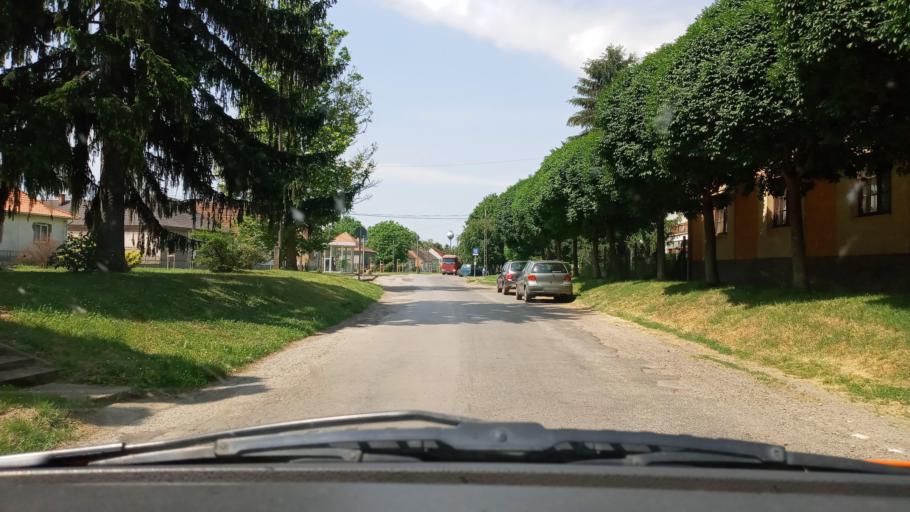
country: HU
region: Baranya
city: Szentlorinc
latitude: 46.0080
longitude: 18.0421
